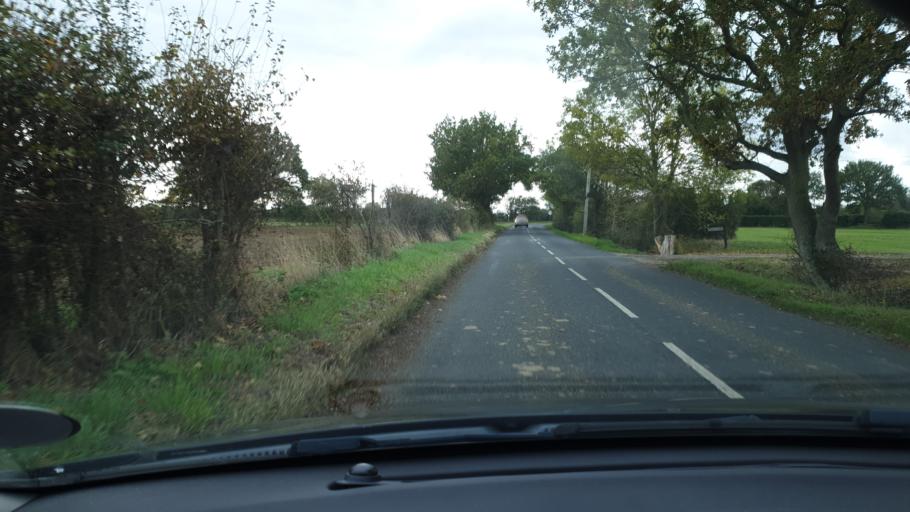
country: GB
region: England
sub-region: Essex
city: Manningtree
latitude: 51.9217
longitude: 1.0474
